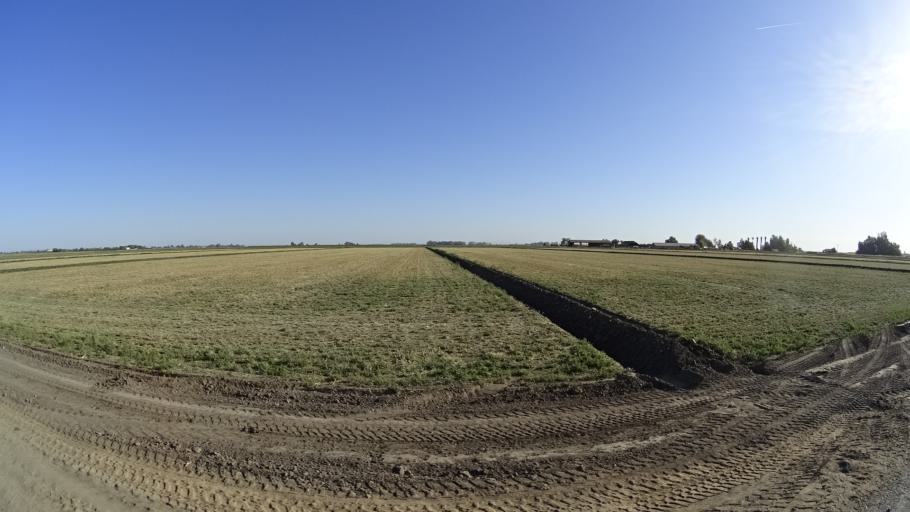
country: US
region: California
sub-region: Kings County
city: Stratford
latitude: 36.1673
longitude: -119.8031
